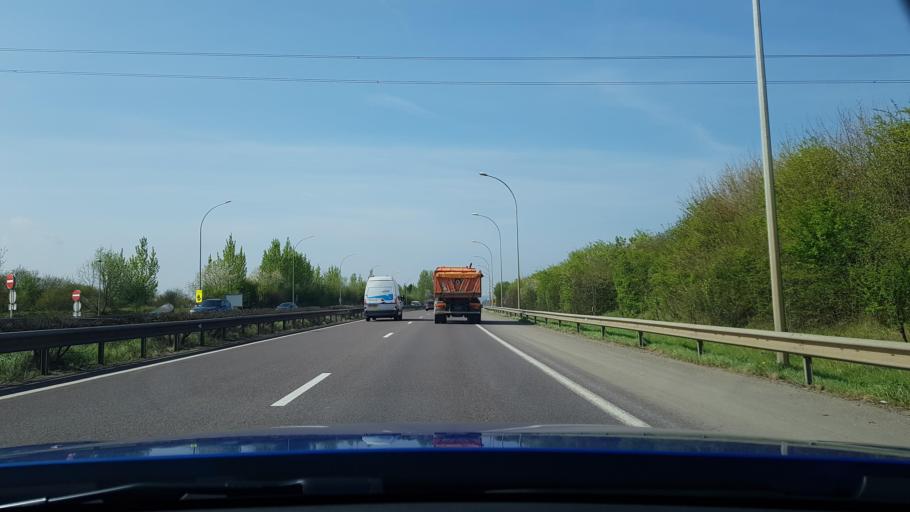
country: LU
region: Luxembourg
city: Pontpierre
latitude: 49.5449
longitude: 6.0399
